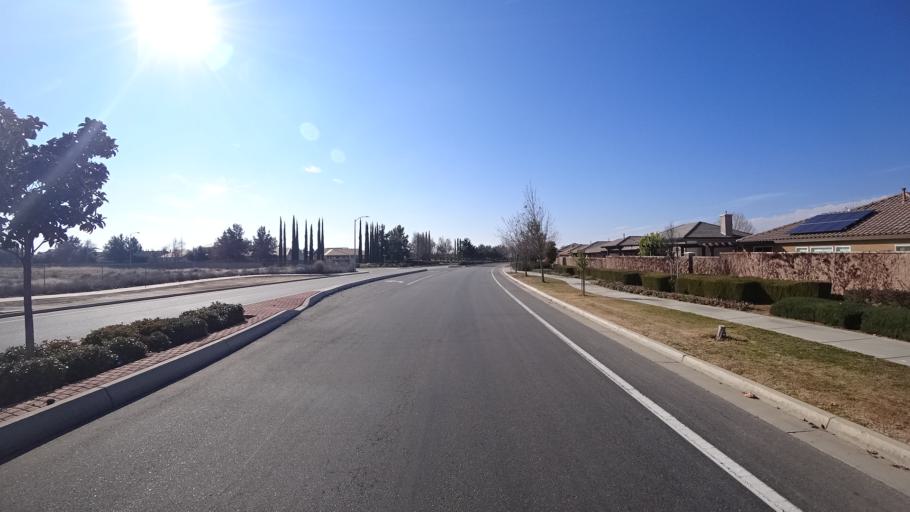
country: US
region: California
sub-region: Kern County
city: Oildale
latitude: 35.4050
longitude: -118.8876
